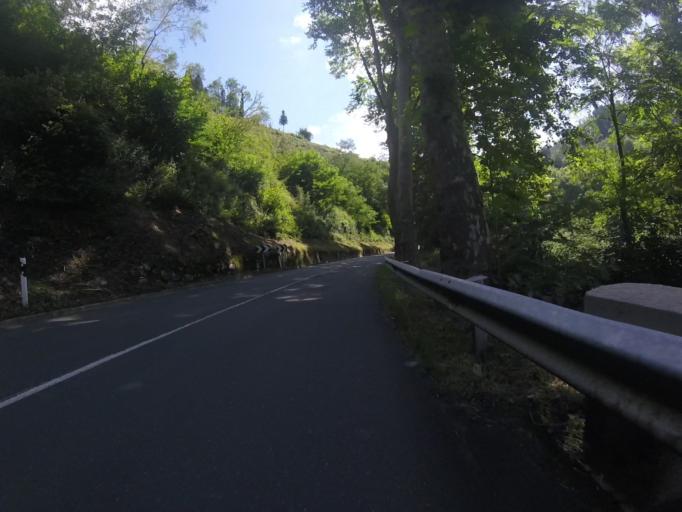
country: ES
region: Basque Country
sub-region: Provincia de Guipuzcoa
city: Azpeitia
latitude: 43.1807
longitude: -2.2269
